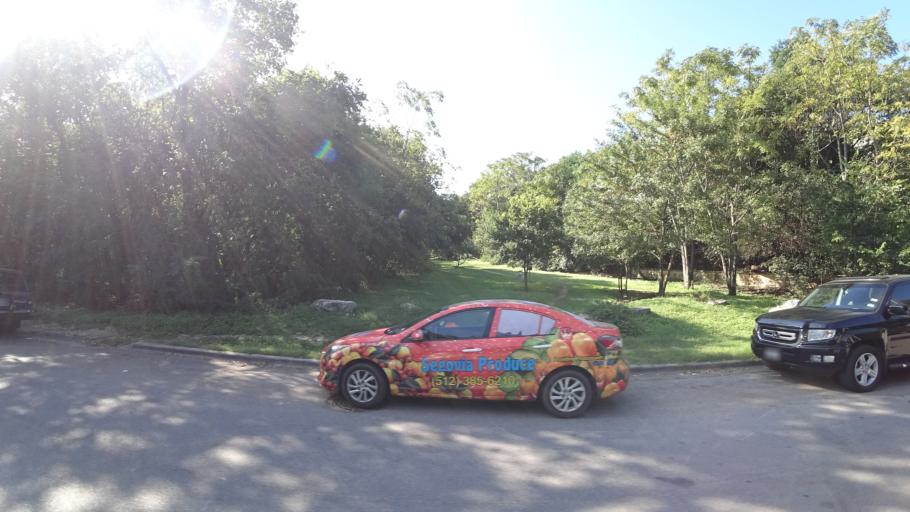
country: US
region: Texas
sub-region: Travis County
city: Austin
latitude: 30.2517
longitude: -97.7467
